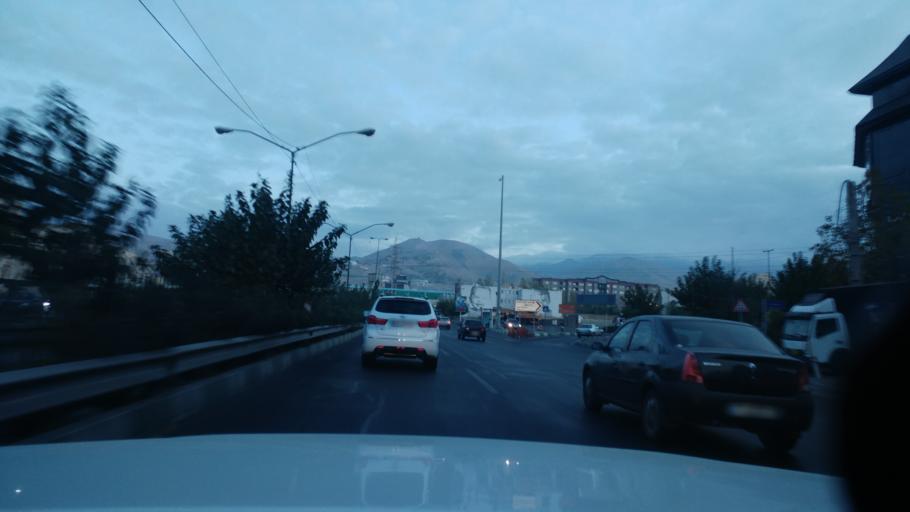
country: IR
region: Tehran
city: Tehran
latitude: 35.7446
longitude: 51.3144
